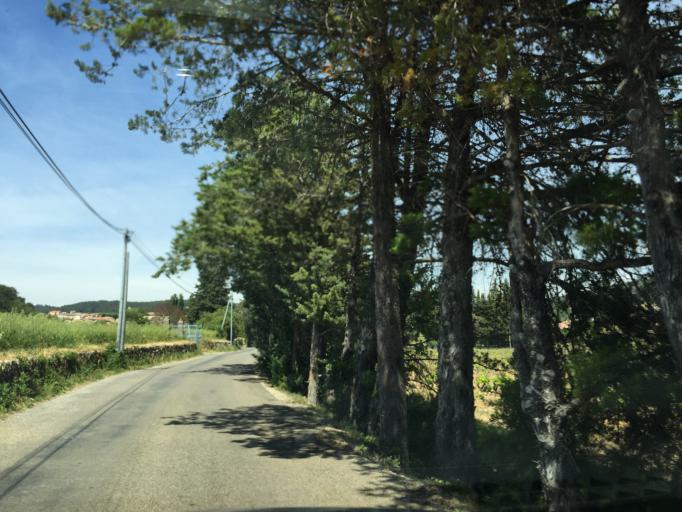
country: FR
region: Provence-Alpes-Cote d'Azur
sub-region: Departement du Var
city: Lorgues
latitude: 43.4849
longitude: 6.3635
